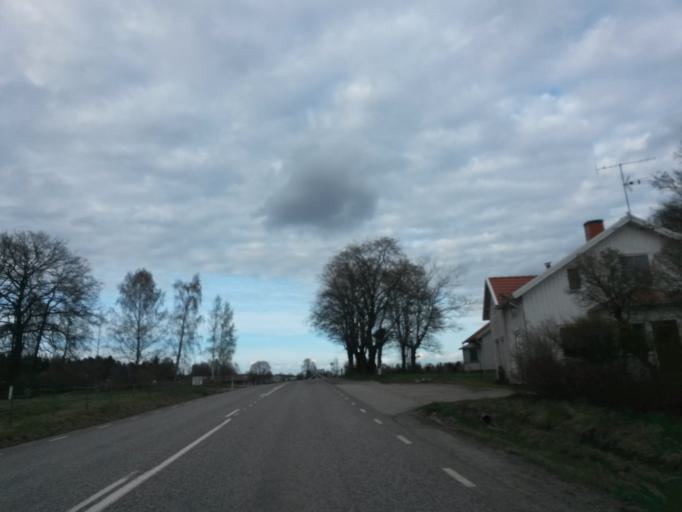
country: SE
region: Vaestra Goetaland
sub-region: Vargarda Kommun
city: Jonstorp
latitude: 58.0403
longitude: 12.6480
